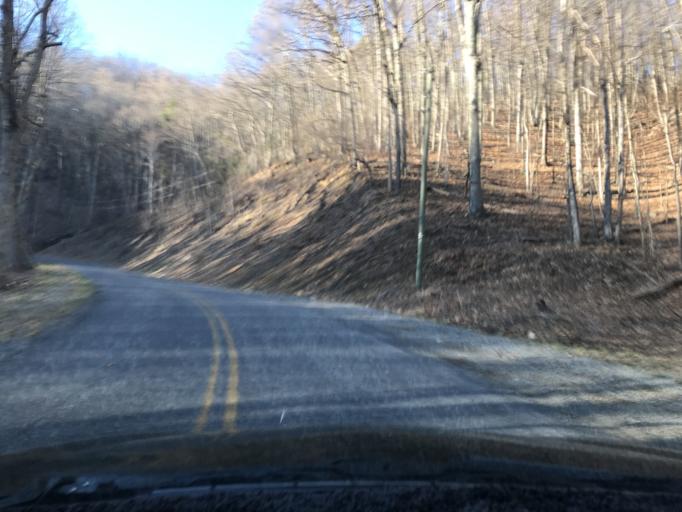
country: US
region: Virginia
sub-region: Botetourt County
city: Buchanan
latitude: 37.4771
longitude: -79.6583
